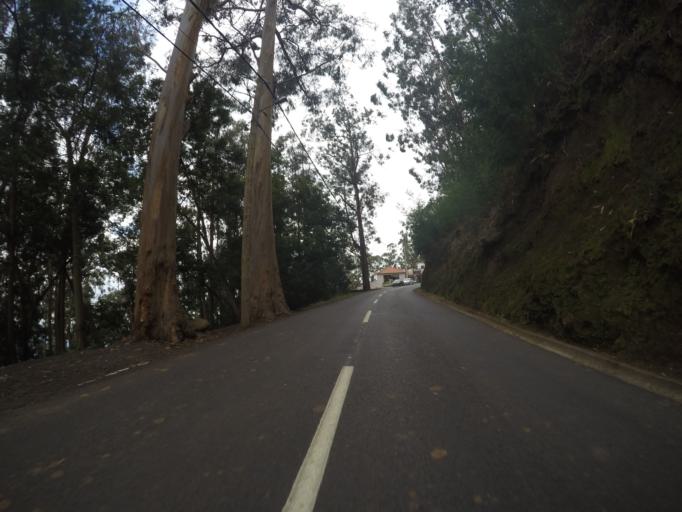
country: PT
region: Madeira
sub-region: Camara de Lobos
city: Curral das Freiras
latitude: 32.6892
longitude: -16.9540
